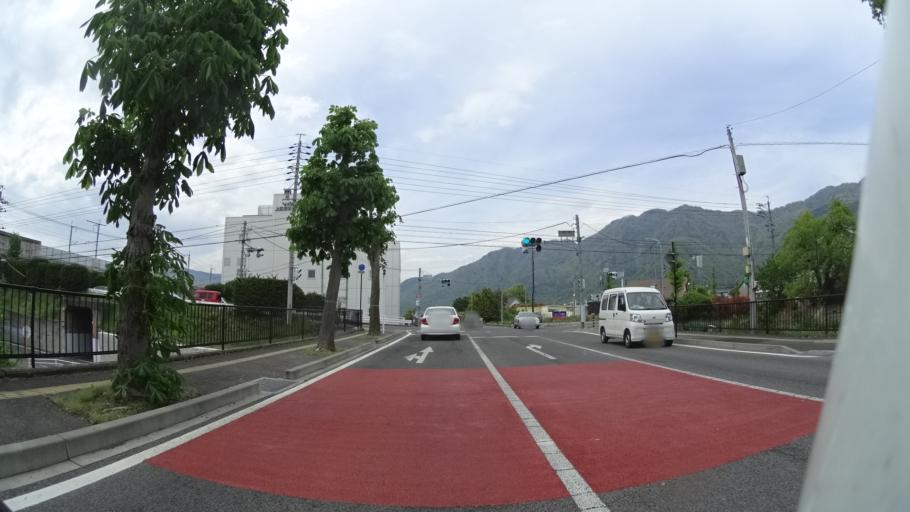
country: JP
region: Nagano
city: Ueda
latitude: 36.4065
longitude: 138.2355
